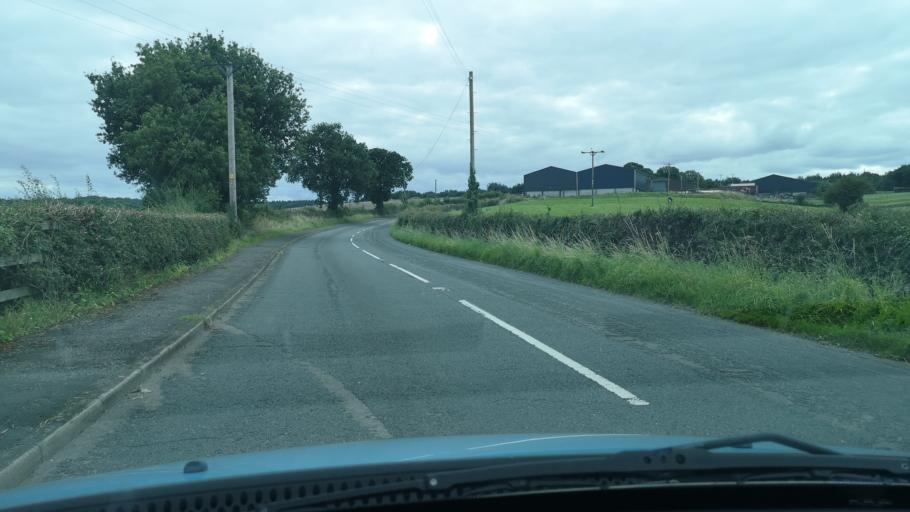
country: GB
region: England
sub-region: City and Borough of Wakefield
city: Crigglestone
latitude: 53.6341
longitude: -1.5459
